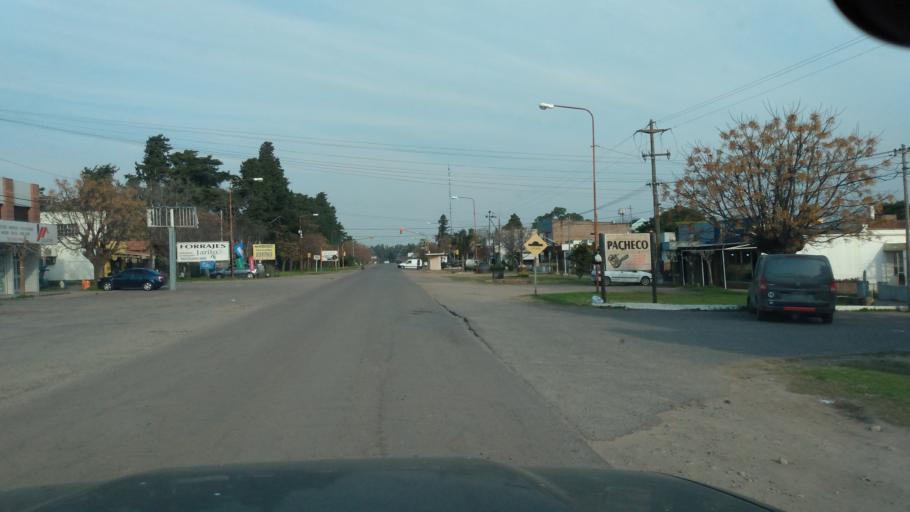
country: AR
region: Buenos Aires
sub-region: Partido de Lujan
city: Lujan
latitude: -34.5736
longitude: -59.1795
